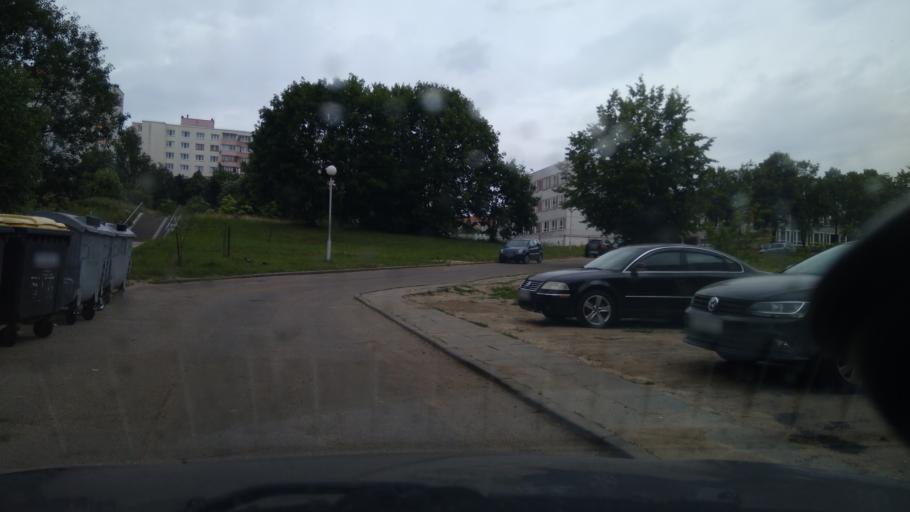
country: BY
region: Minsk
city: Novoye Medvezhino
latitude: 53.8941
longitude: 27.4451
